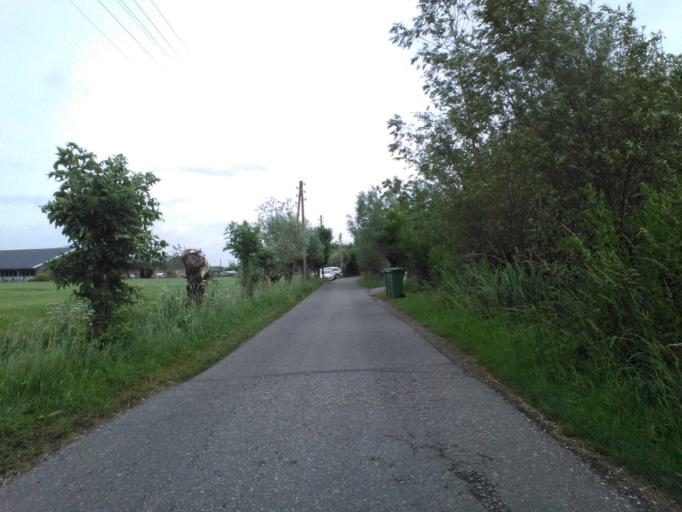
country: NL
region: South Holland
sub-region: Gemeente Vlist
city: Haastrecht
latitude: 51.9585
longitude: 4.7653
